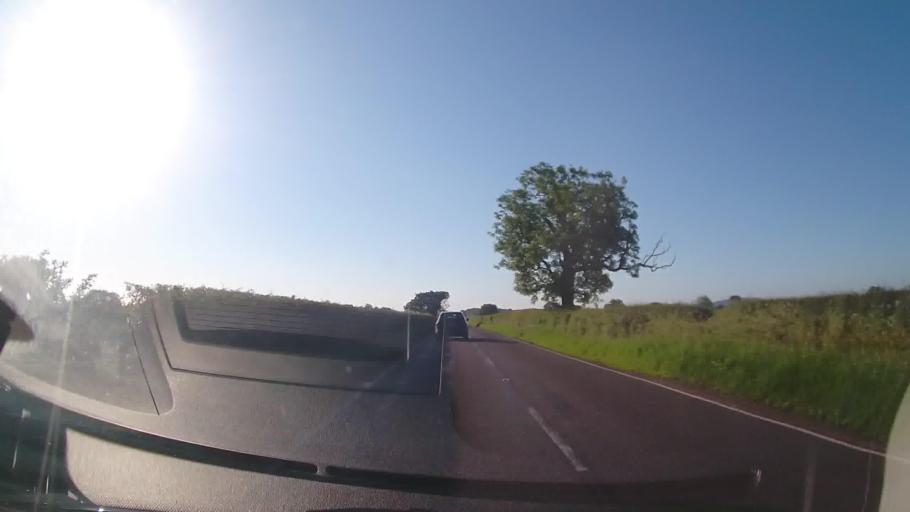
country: GB
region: England
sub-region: Shropshire
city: Shawbury
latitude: 52.7658
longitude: -2.6320
